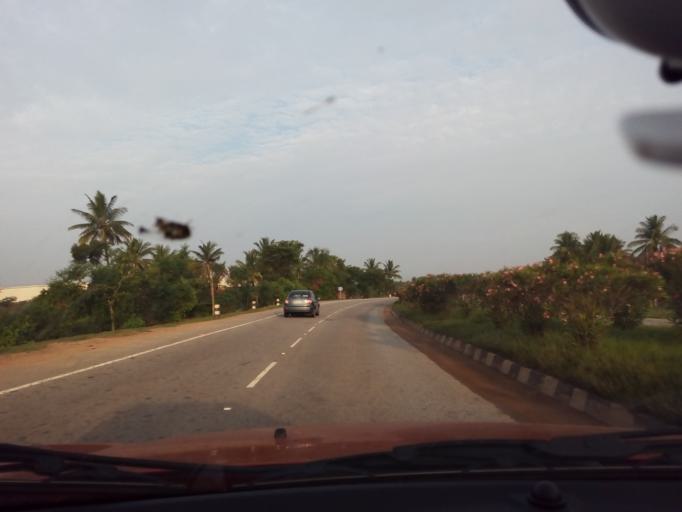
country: IN
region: Karnataka
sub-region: Ramanagara
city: Magadi
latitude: 13.0639
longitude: 77.2625
